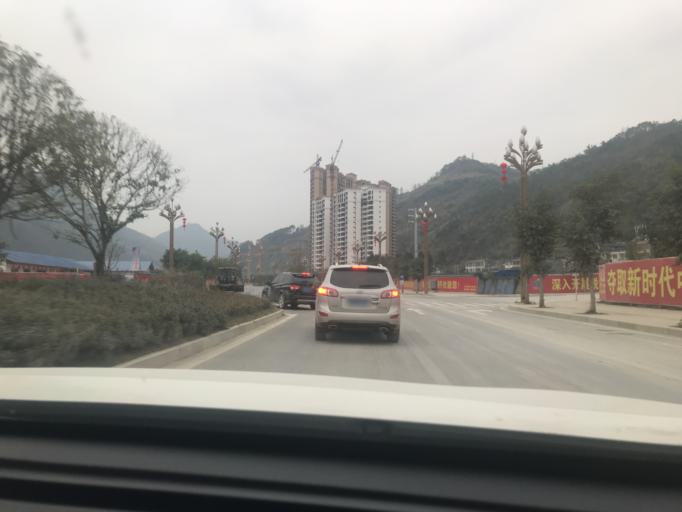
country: CN
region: Guangxi Zhuangzu Zizhiqu
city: Xinzhou
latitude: 24.9929
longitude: 105.7763
